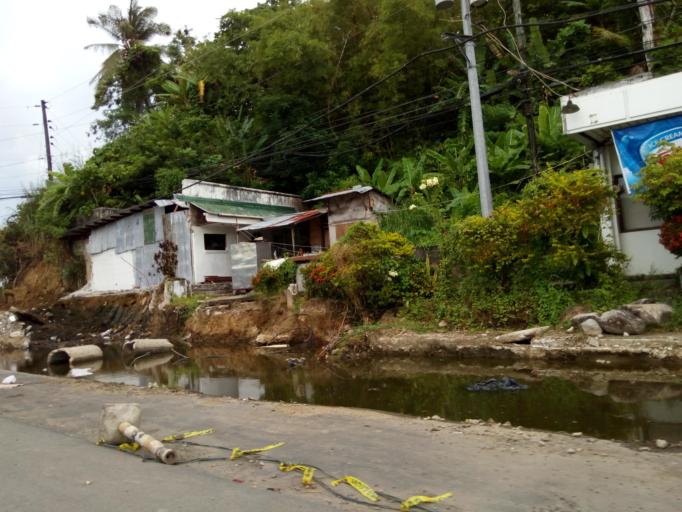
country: PH
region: Caraga
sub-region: Province of Surigao del Norte
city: Surigao
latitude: 9.7822
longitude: 125.4863
